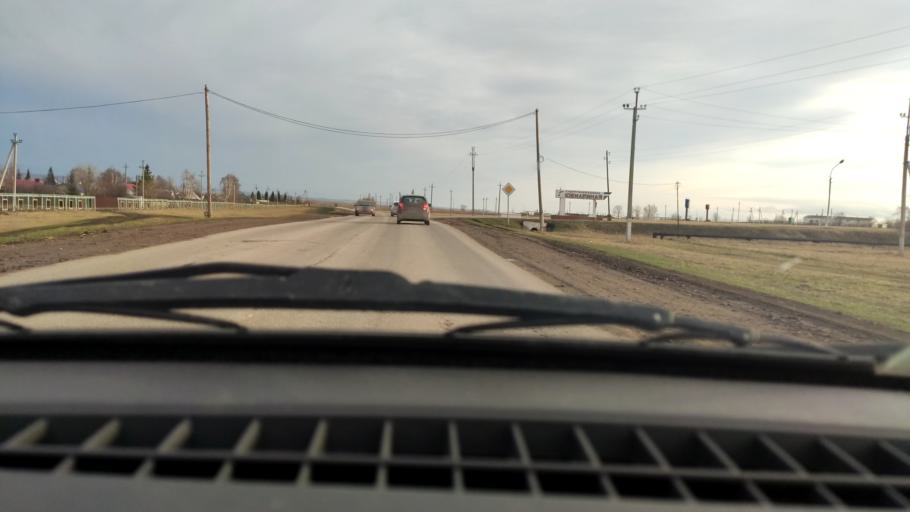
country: RU
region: Bashkortostan
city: Davlekanovo
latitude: 54.3819
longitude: 55.1959
